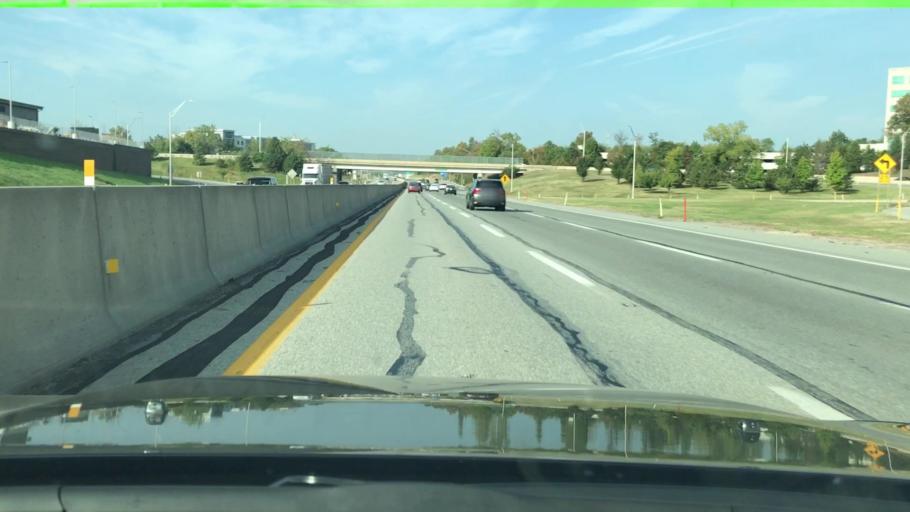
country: US
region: Pennsylvania
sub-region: Montgomery County
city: Plymouth Meeting
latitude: 40.1110
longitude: -75.2875
